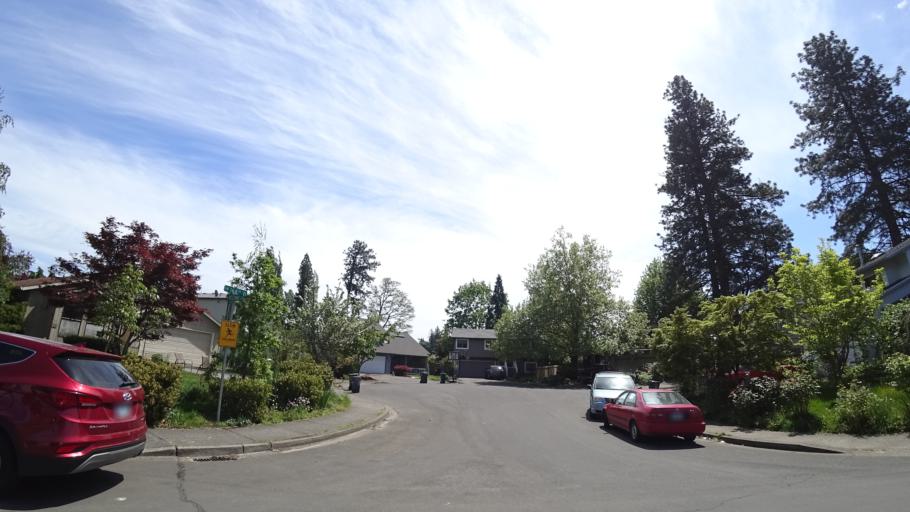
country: US
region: Oregon
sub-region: Washington County
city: Aloha
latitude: 45.4874
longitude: -122.8459
